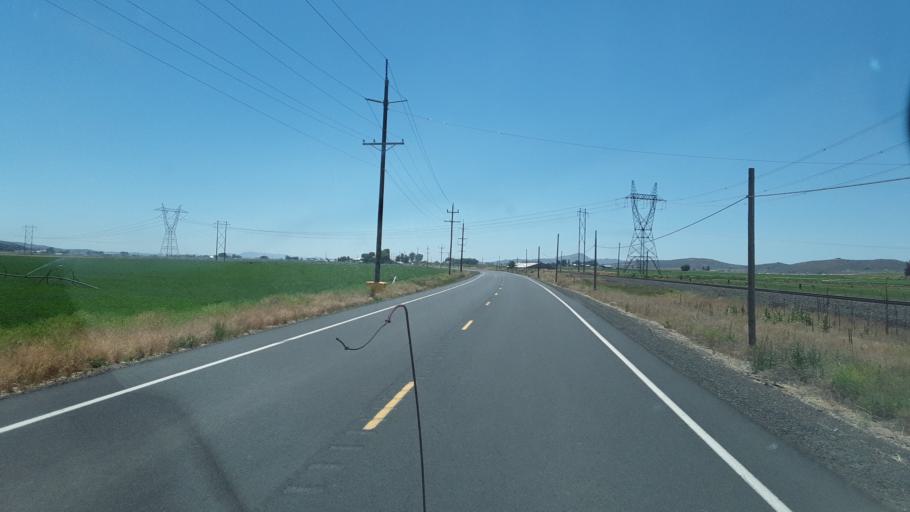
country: US
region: Oregon
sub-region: Klamath County
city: Altamont
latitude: 42.0781
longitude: -121.6752
